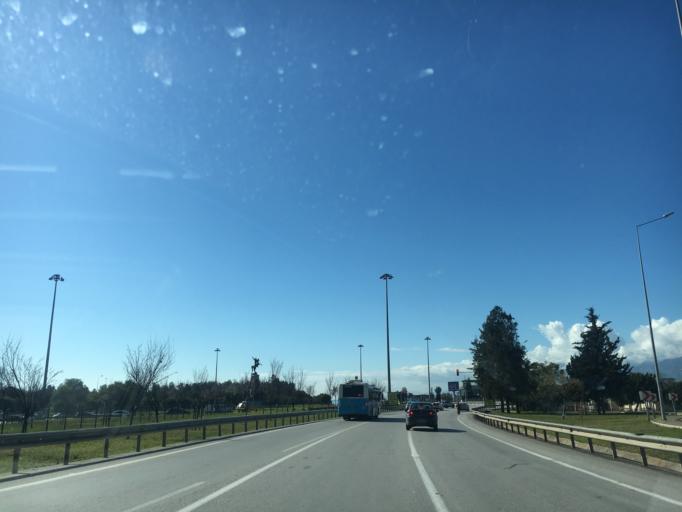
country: TR
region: Antalya
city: Antalya
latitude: 36.8867
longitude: 30.6631
